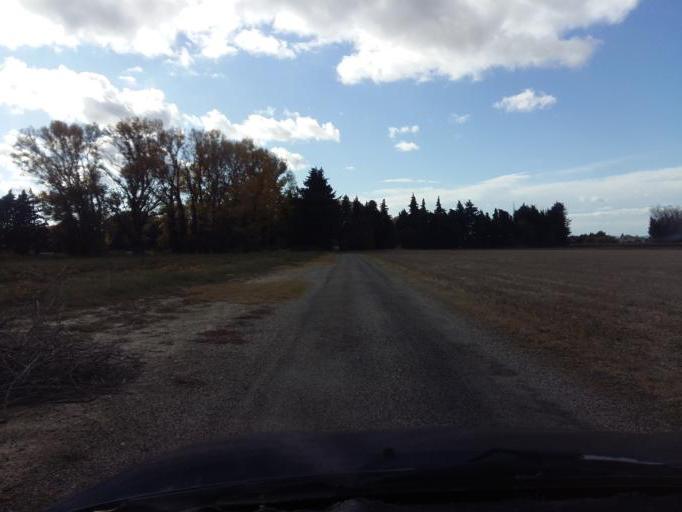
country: FR
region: Provence-Alpes-Cote d'Azur
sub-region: Departement du Vaucluse
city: Camaret-sur-Aigues
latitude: 44.1538
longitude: 4.8465
